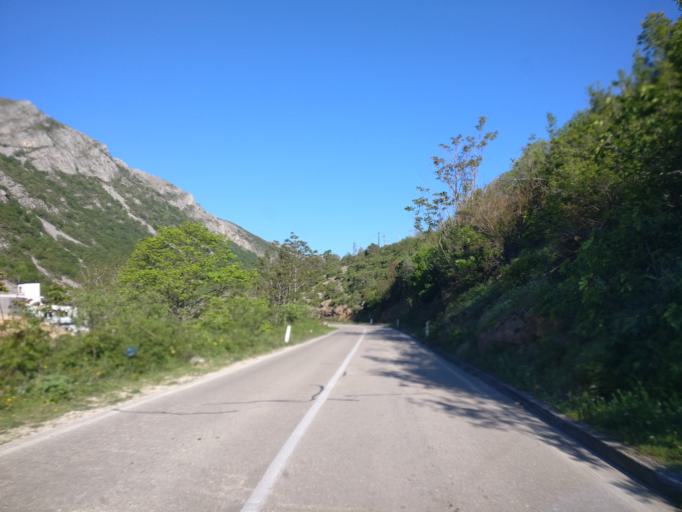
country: BA
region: Federation of Bosnia and Herzegovina
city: Stolac
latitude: 43.0782
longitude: 18.0197
